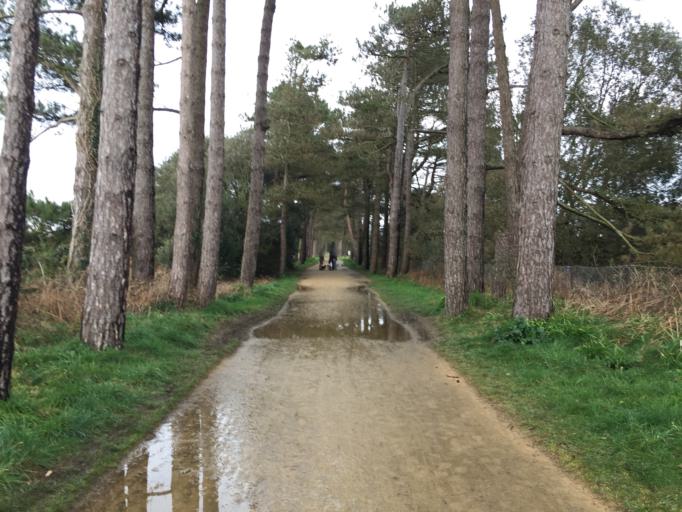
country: JE
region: St Helier
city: Saint Helier
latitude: 49.1903
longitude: -2.2147
